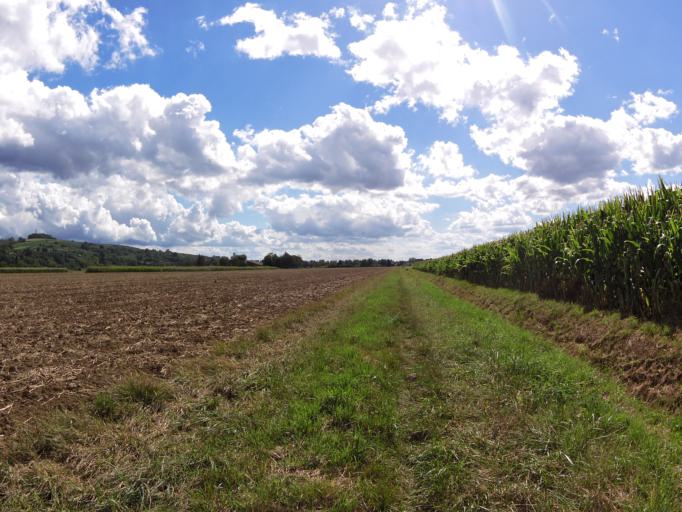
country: DE
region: Baden-Wuerttemberg
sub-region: Freiburg Region
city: Lahr
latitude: 48.3665
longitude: 7.8477
